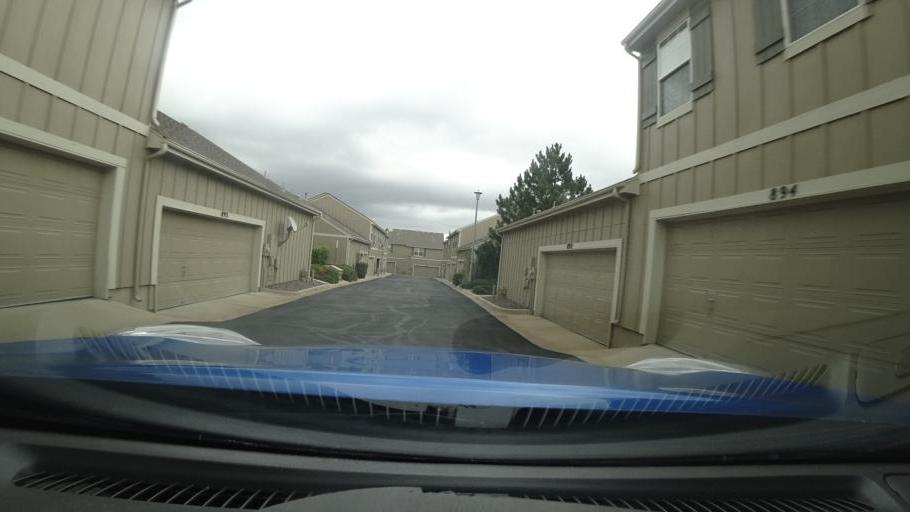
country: US
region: Colorado
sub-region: Adams County
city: Aurora
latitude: 39.7002
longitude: -104.8112
